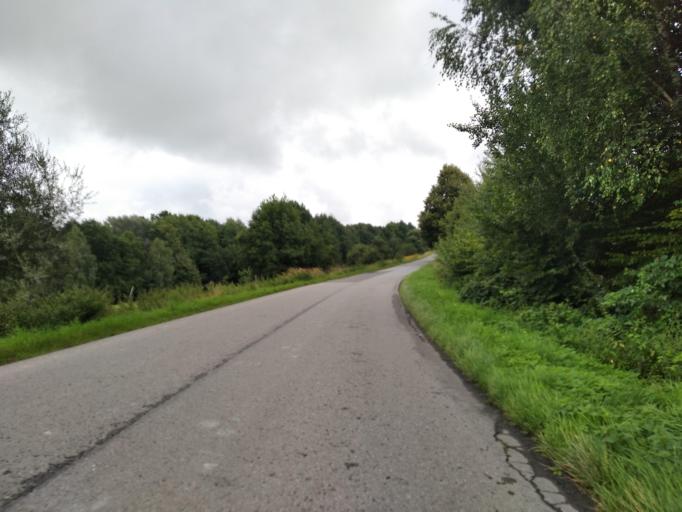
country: PL
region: Subcarpathian Voivodeship
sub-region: Powiat rzeszowski
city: Dynow
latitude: 49.7261
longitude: 22.3086
